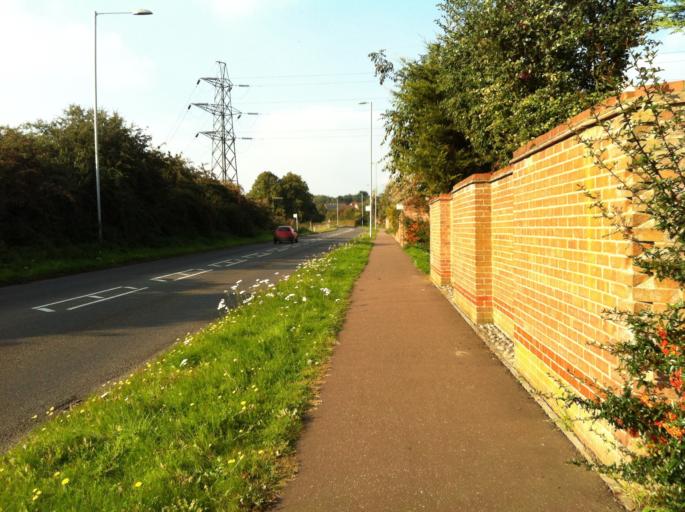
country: GB
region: England
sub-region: Norfolk
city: Bowthorpe
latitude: 52.6335
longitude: 1.2149
